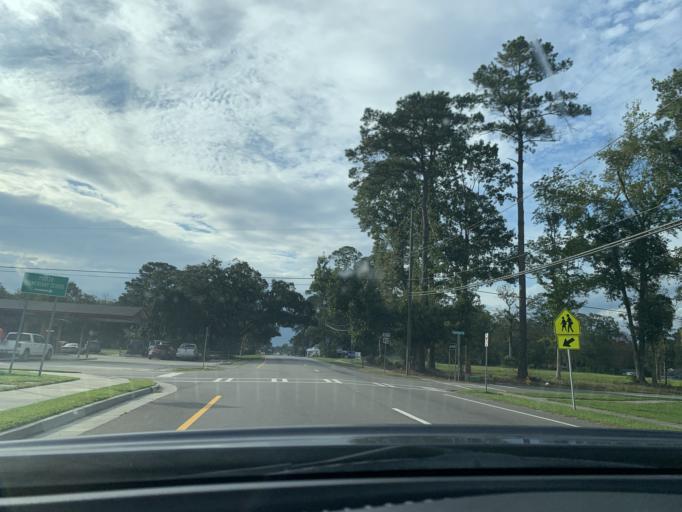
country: US
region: Georgia
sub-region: Chatham County
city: Pooler
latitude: 32.1167
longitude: -81.2507
